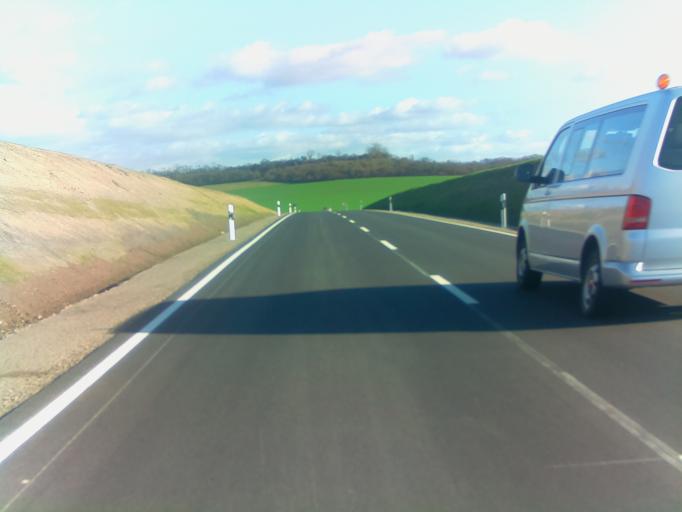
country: DE
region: Bavaria
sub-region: Regierungsbezirk Unterfranken
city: Herbstadt
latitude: 50.3112
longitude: 10.5025
